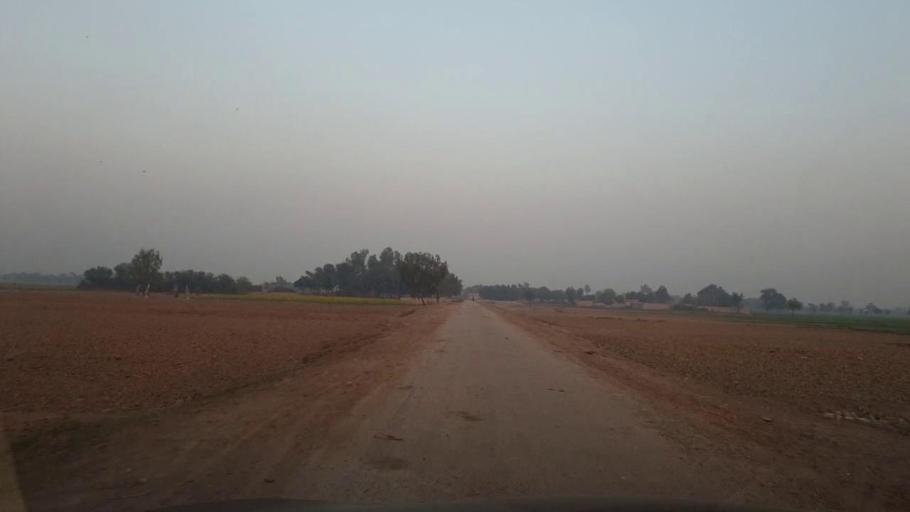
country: PK
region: Sindh
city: Ubauro
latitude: 28.2737
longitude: 69.7846
